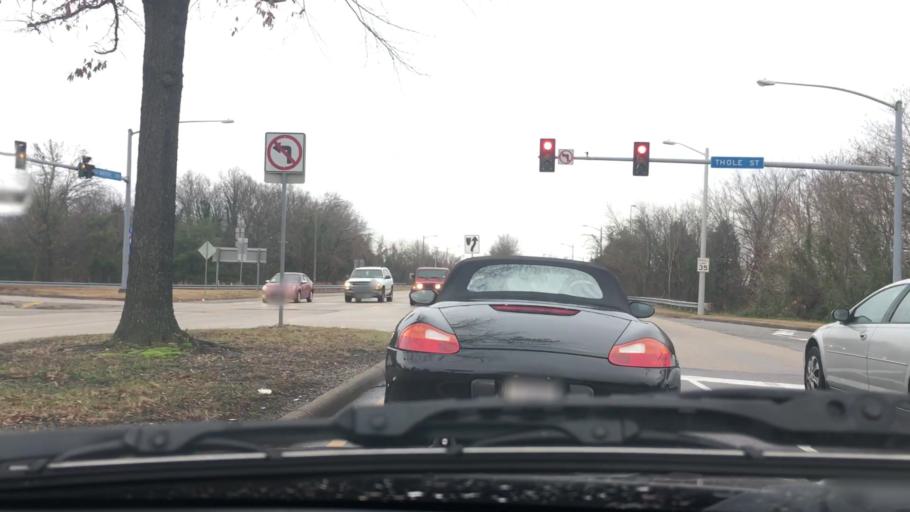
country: US
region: Virginia
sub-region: City of Norfolk
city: Norfolk
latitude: 36.9047
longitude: -76.2566
